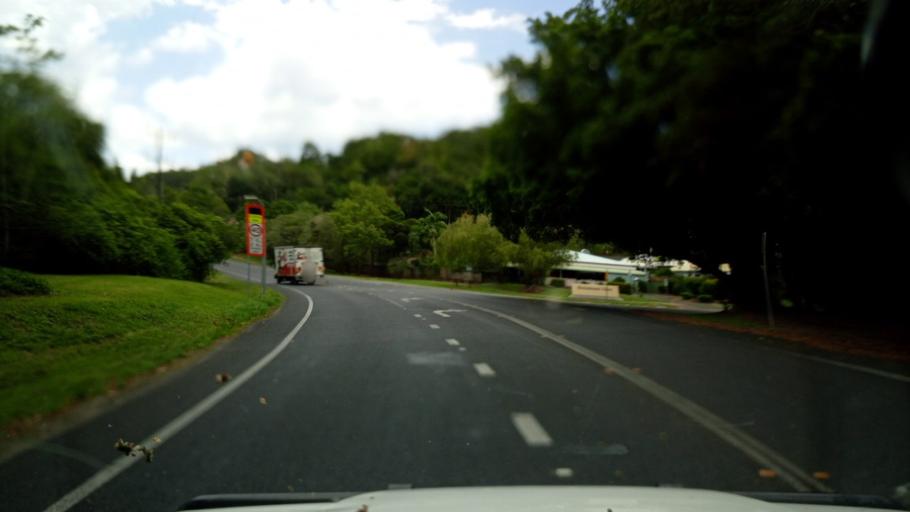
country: AU
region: Queensland
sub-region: Cairns
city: Redlynch
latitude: -16.8941
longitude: 145.7108
